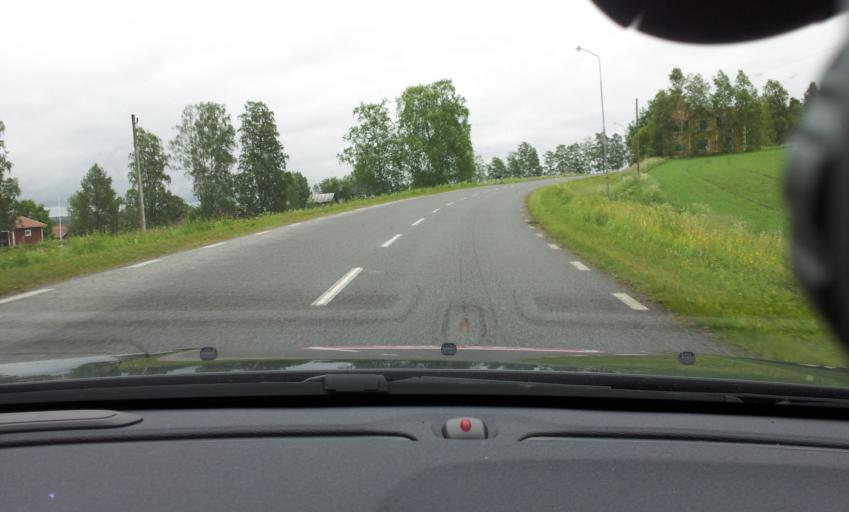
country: SE
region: Jaemtland
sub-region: Stroemsunds Kommun
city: Stroemsund
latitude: 63.6296
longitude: 15.2311
